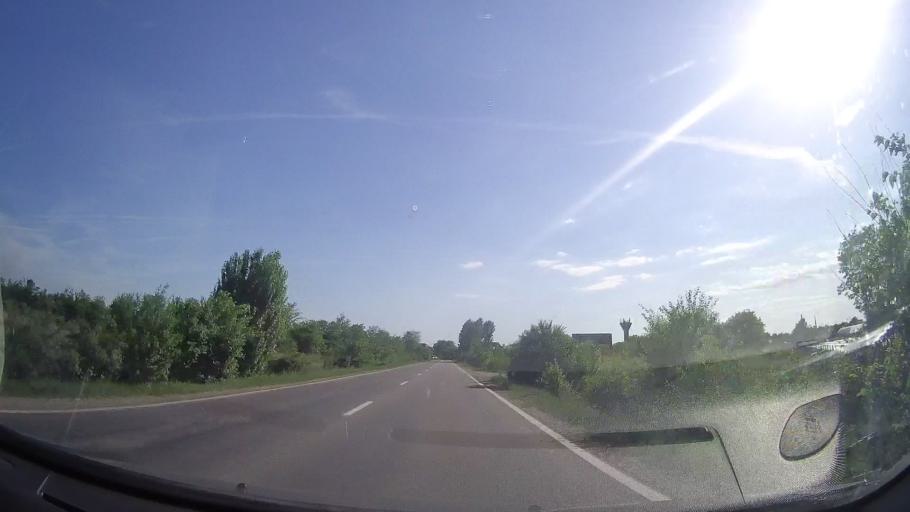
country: RO
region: Prahova
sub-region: Comuna Barcanesti
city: Barcanesti
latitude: 44.8909
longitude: 26.0486
